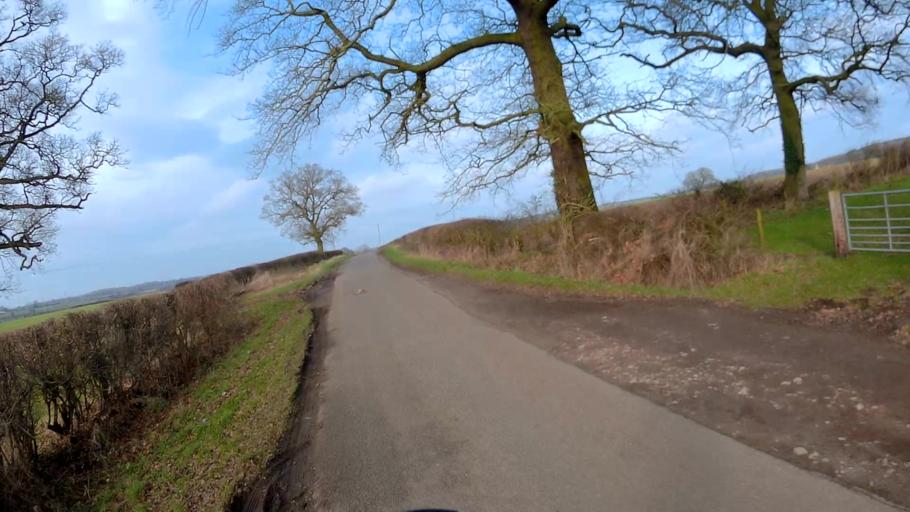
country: GB
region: England
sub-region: Lincolnshire
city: Bourne
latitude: 52.7660
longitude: -0.4212
